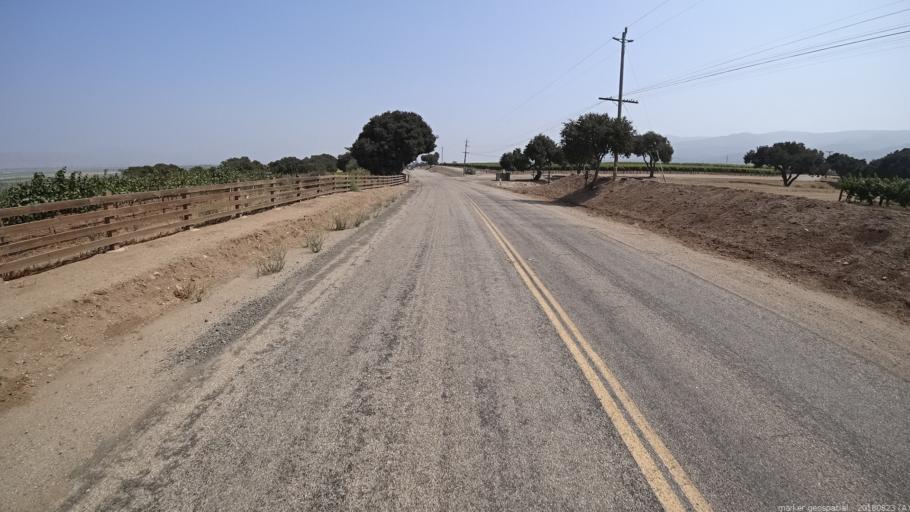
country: US
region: California
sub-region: Monterey County
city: Gonzales
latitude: 36.4560
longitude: -121.4453
